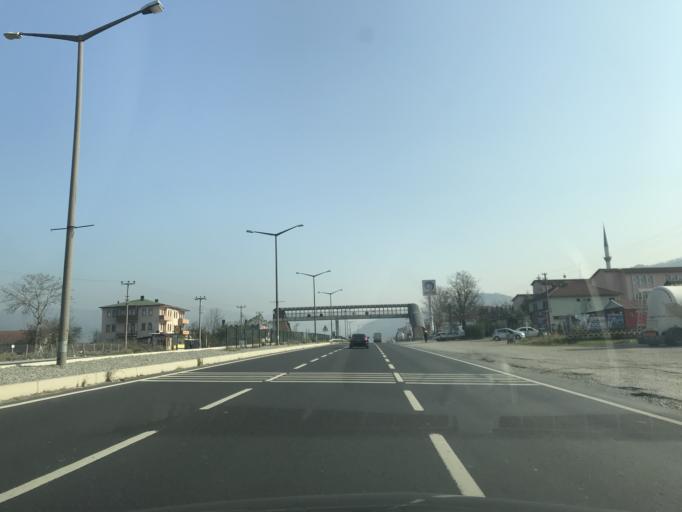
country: TR
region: Duzce
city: Kaynasli
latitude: 40.7766
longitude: 31.3007
